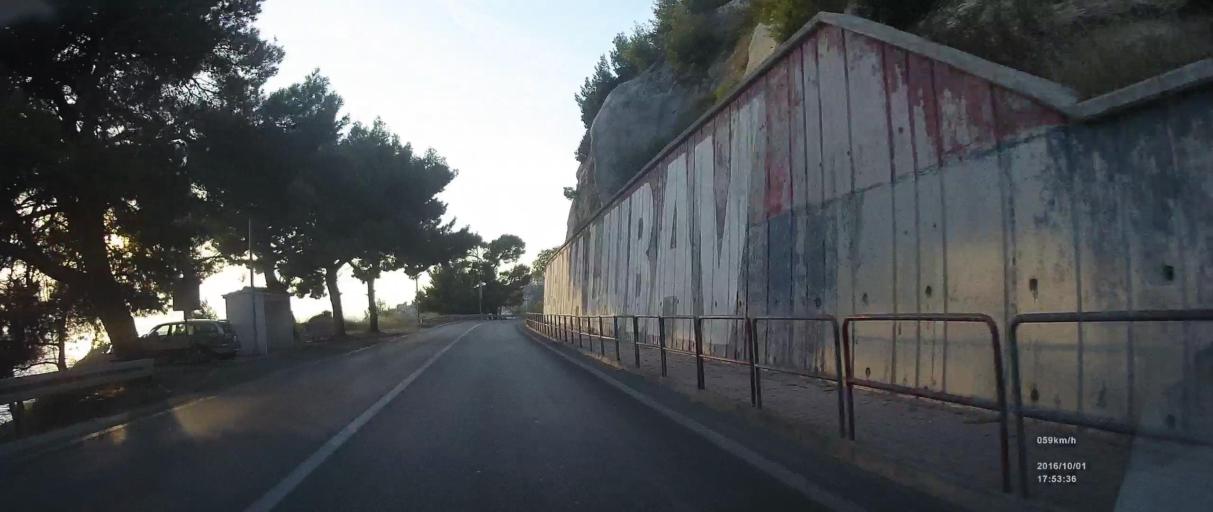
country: HR
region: Splitsko-Dalmatinska
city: Jesenice
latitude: 43.4585
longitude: 16.6079
